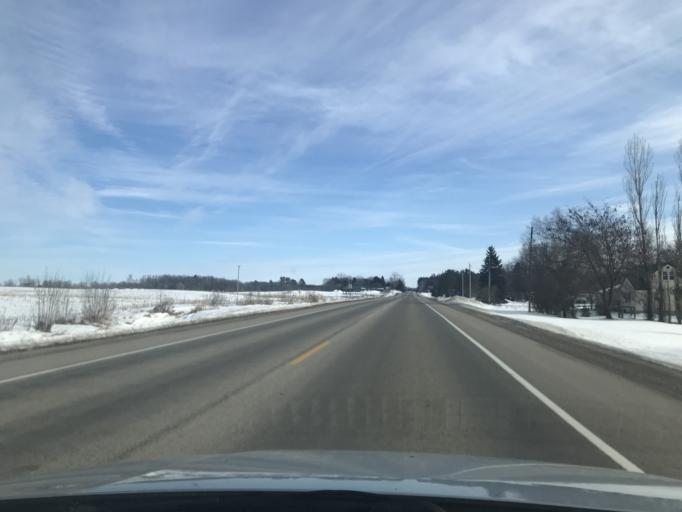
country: US
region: Wisconsin
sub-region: Oconto County
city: Gillett
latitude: 44.8968
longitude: -88.2991
